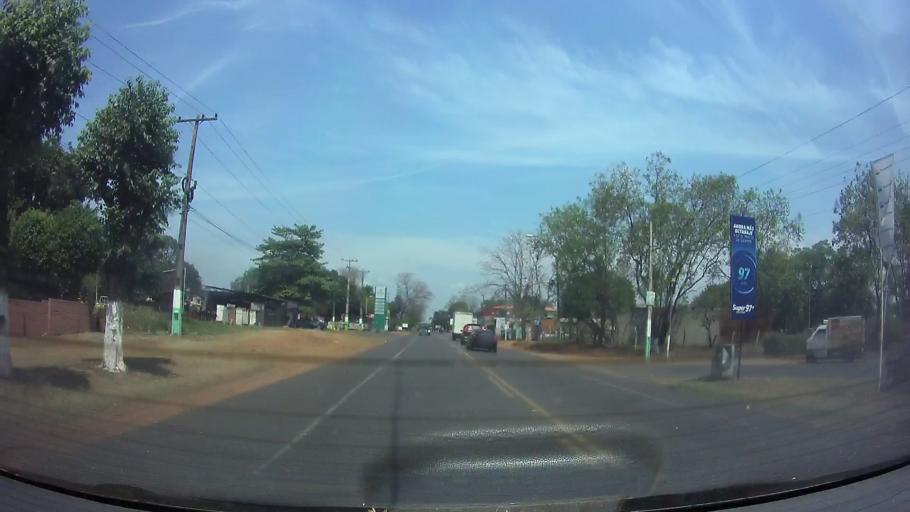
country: PY
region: Central
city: Guarambare
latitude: -25.4343
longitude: -57.4476
